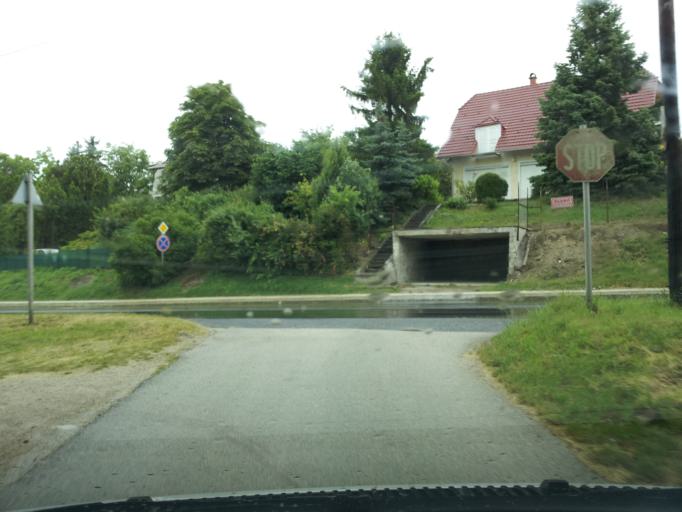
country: HU
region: Veszprem
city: Balatonkenese
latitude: 47.0211
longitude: 18.1505
